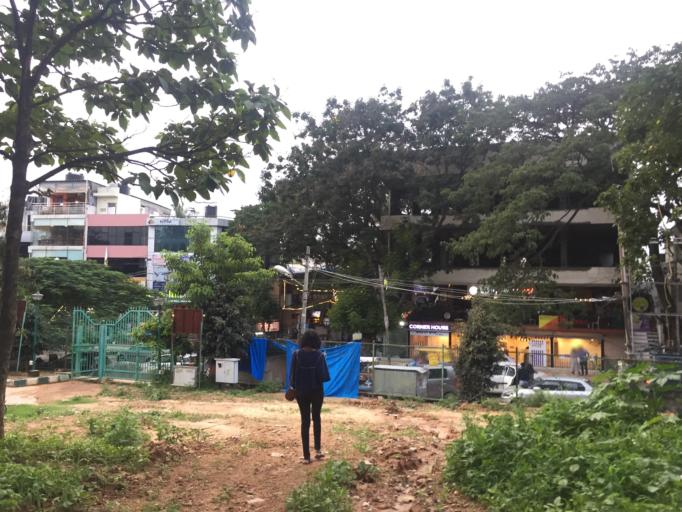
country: IN
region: Karnataka
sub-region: Bangalore Urban
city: Bangalore
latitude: 12.9334
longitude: 77.6198
